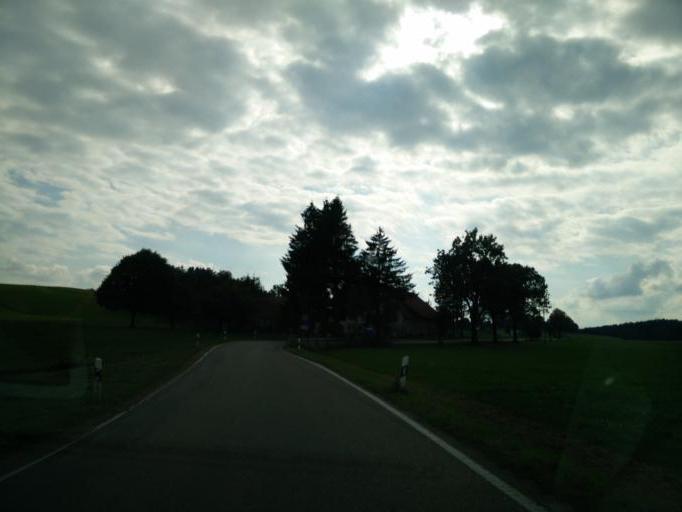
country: DE
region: Baden-Wuerttemberg
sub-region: Tuebingen Region
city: Bad Wurzach
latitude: 47.8515
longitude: 9.8879
